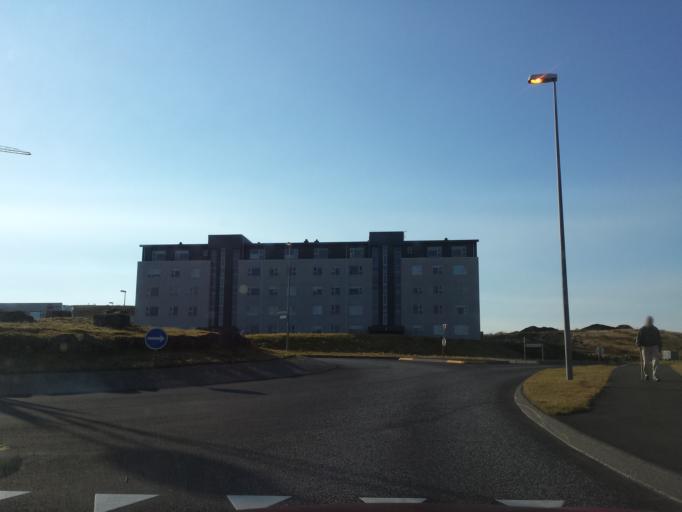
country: IS
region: Capital Region
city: Reykjavik
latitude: 64.0820
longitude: -21.8178
